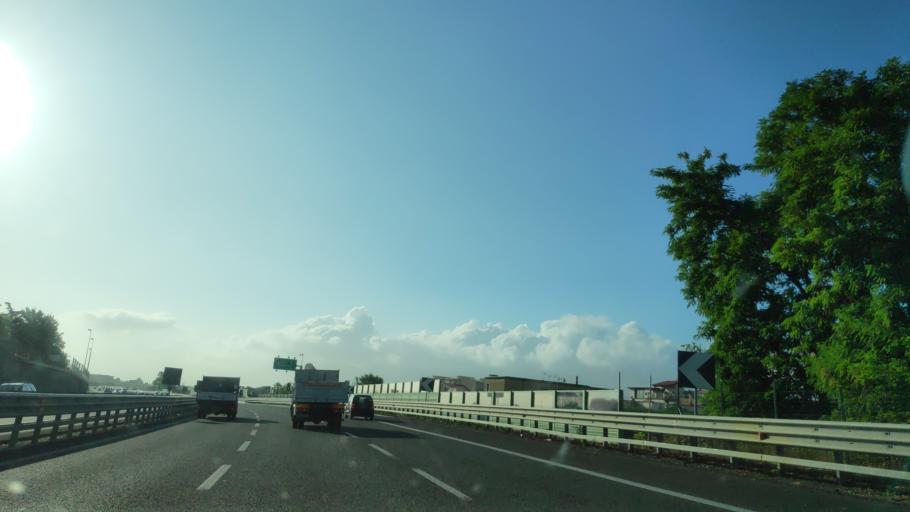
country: IT
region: Campania
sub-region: Provincia di Napoli
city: Trecase
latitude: 40.7622
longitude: 14.4429
